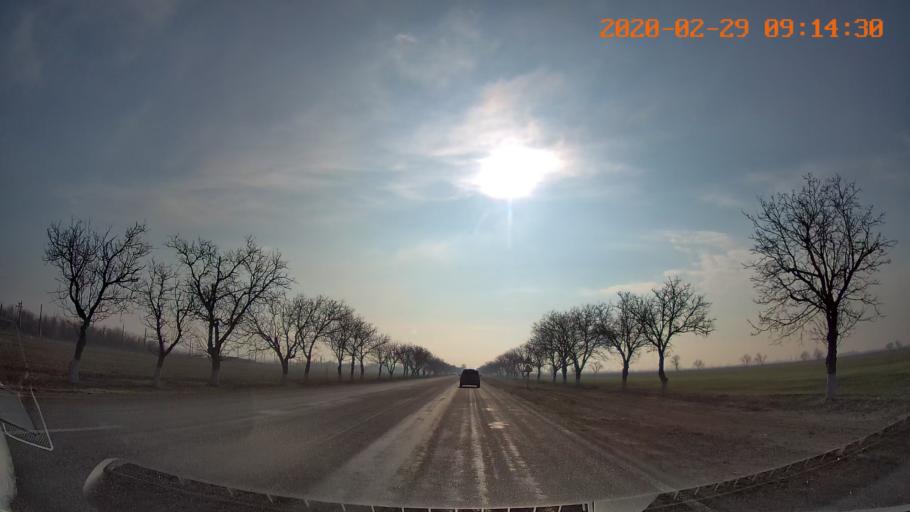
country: MD
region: Telenesti
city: Pervomaisc
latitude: 46.8081
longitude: 29.8539
